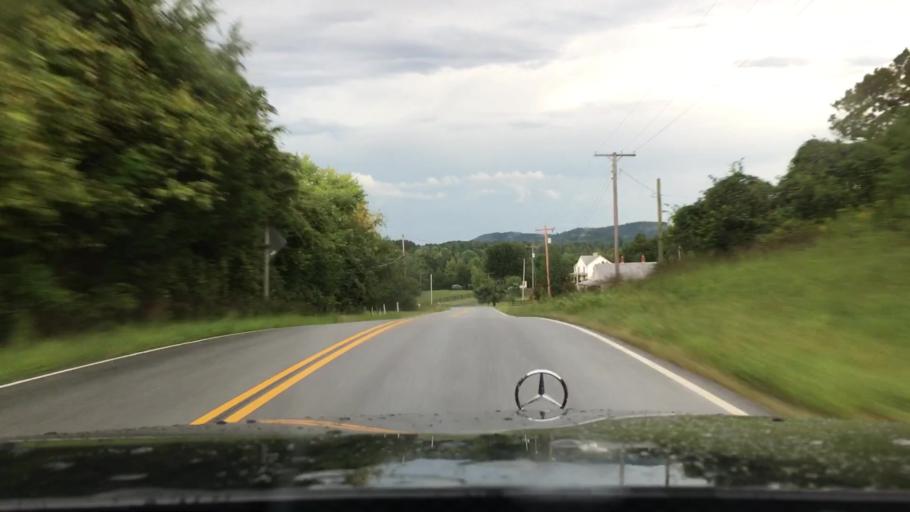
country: US
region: Virginia
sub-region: Amherst County
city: Amherst
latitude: 37.7128
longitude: -79.0231
